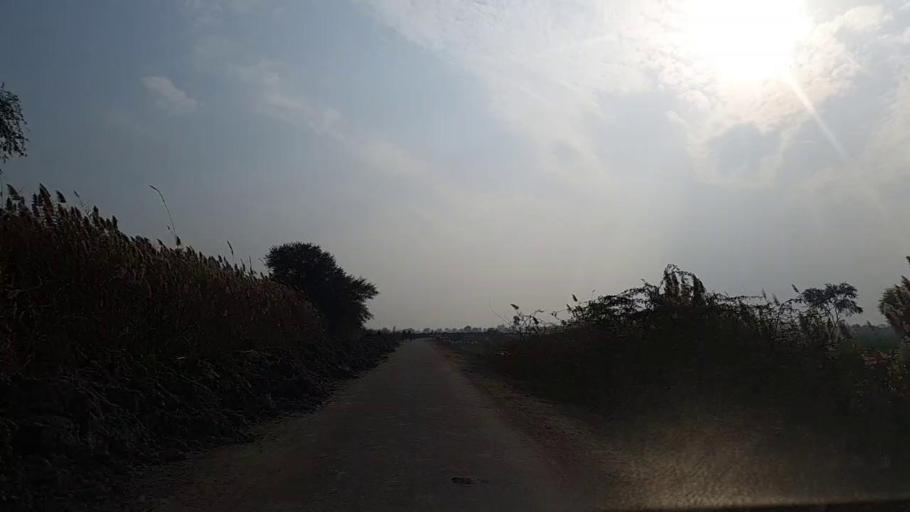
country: PK
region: Sindh
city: Jam Sahib
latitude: 26.3093
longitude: 68.5224
